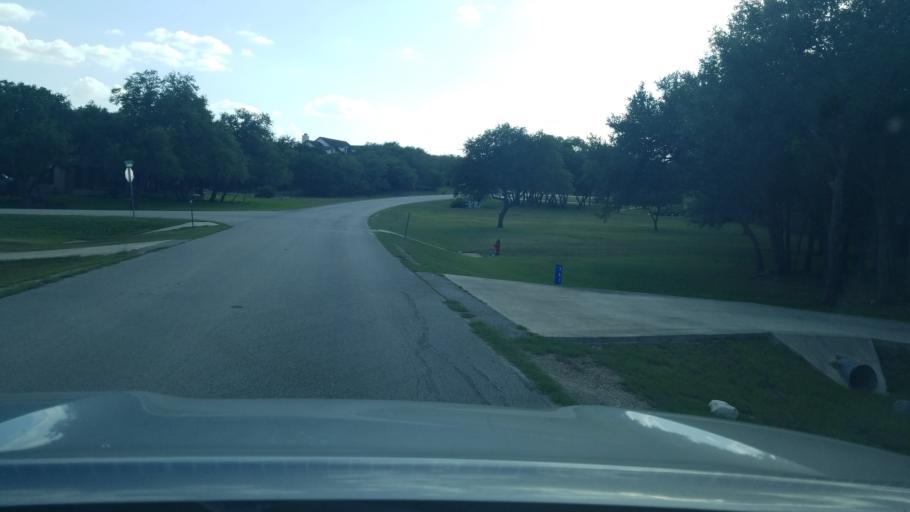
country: US
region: Texas
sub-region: Comal County
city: Bulverde
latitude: 29.8059
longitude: -98.4039
